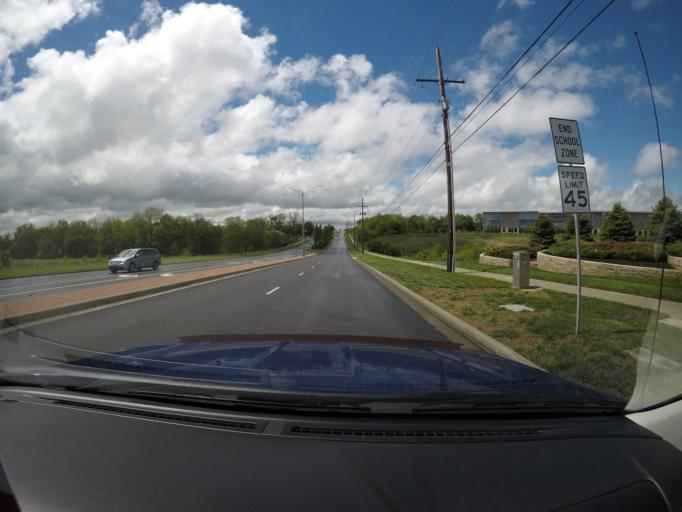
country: US
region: Kansas
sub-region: Johnson County
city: Olathe
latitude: 38.9274
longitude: -94.8408
